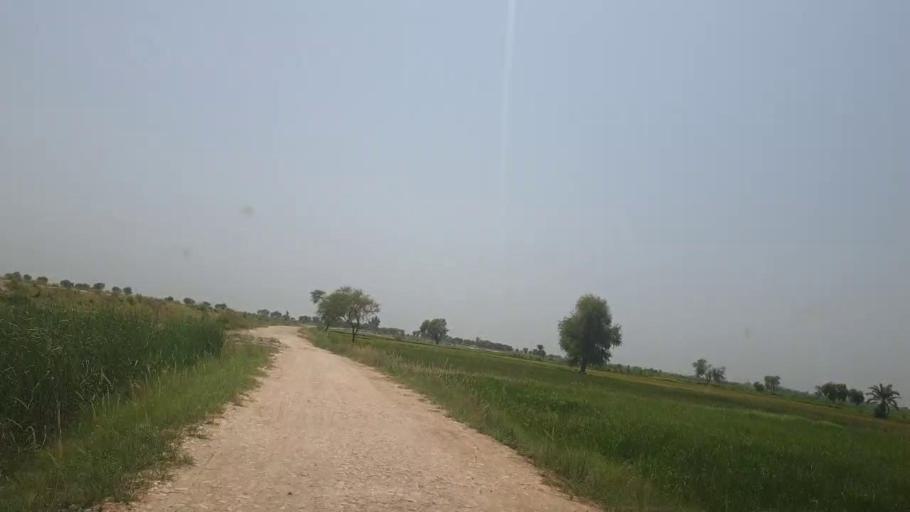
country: PK
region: Sindh
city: Lakhi
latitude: 27.8560
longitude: 68.6649
